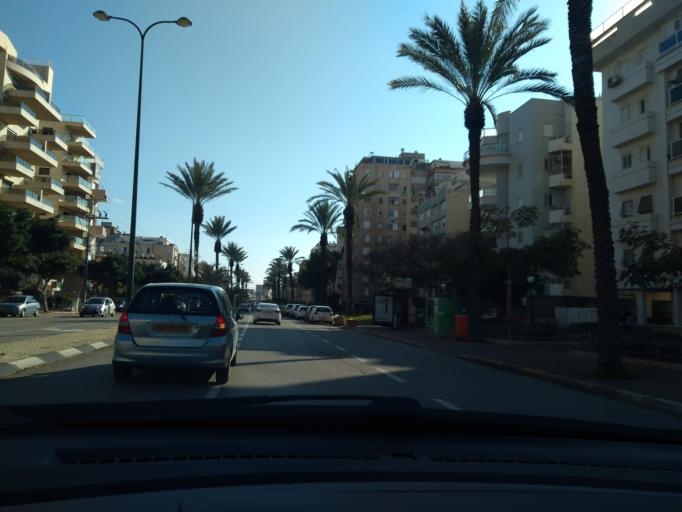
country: IL
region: Central District
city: Netanya
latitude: 32.3349
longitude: 34.8593
